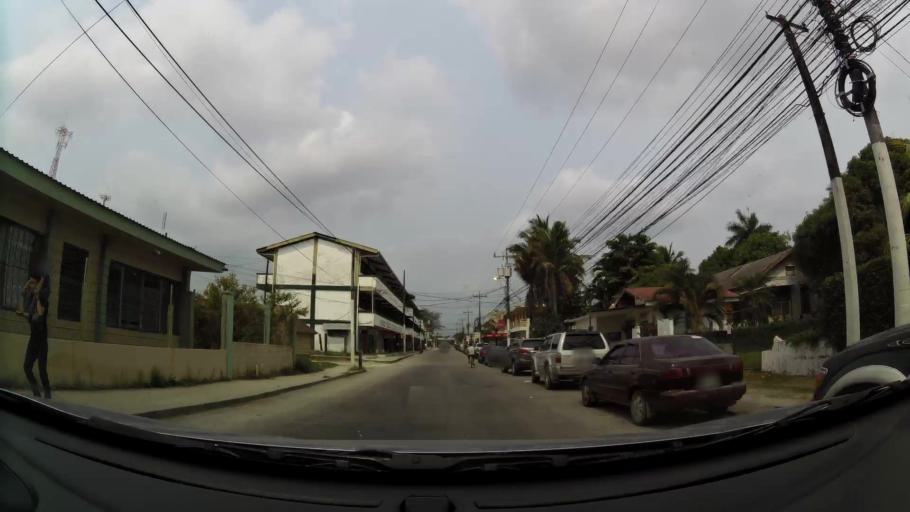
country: HN
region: Atlantida
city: Tela
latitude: 15.7805
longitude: -87.4563
